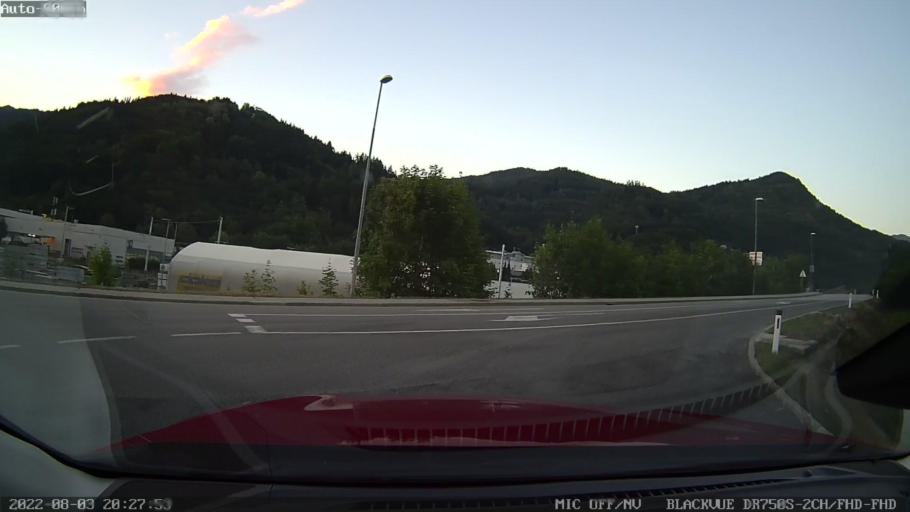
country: SI
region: Jesenice
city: Hrusica
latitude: 46.4404
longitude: 14.0342
